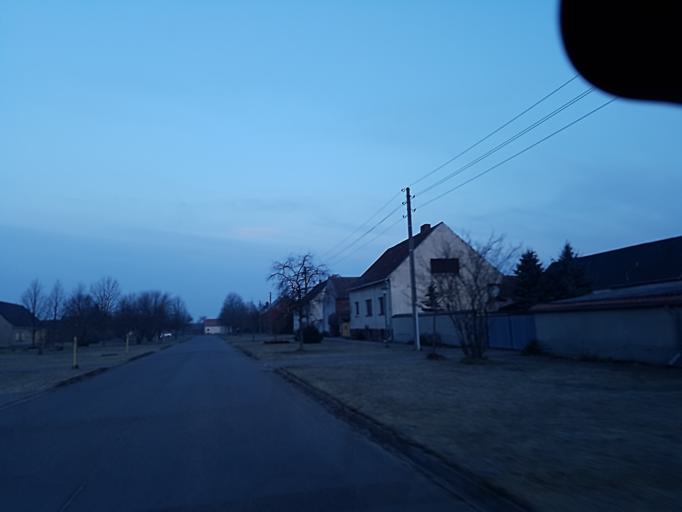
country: DE
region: Brandenburg
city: Herzberg
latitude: 51.7365
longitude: 13.2049
